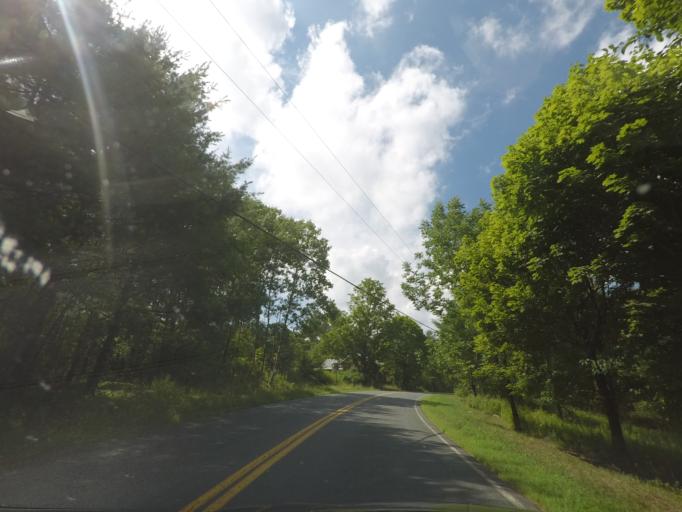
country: US
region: New York
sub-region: Rensselaer County
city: Averill Park
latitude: 42.6045
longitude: -73.5532
